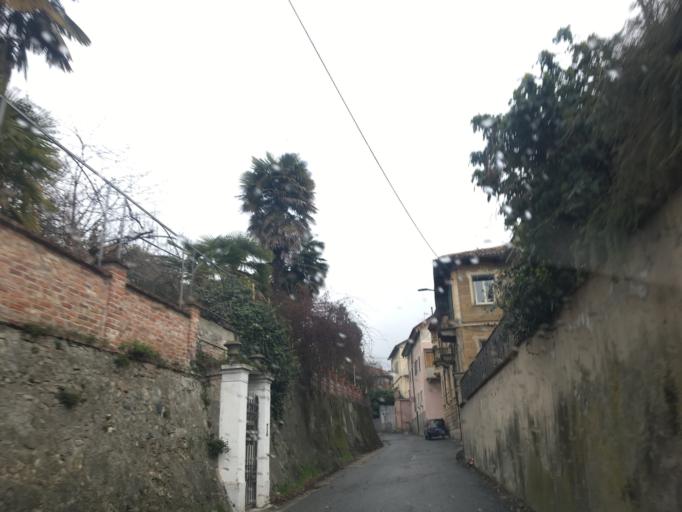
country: IT
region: Piedmont
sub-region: Provincia di Torino
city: Moncalieri
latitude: 45.0272
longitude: 7.6849
